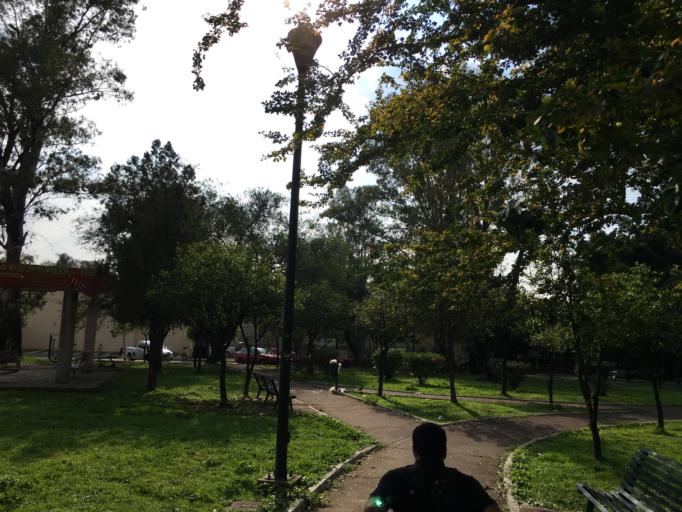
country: MX
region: Jalisco
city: Guadalajara
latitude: 20.6496
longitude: -103.3940
